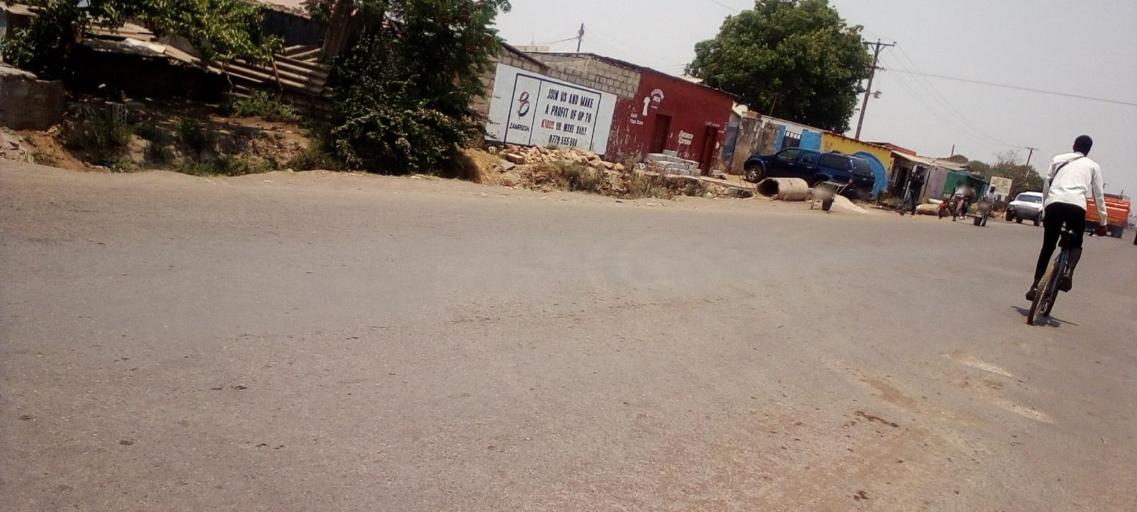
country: ZM
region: Lusaka
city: Lusaka
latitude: -15.4422
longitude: 28.2510
